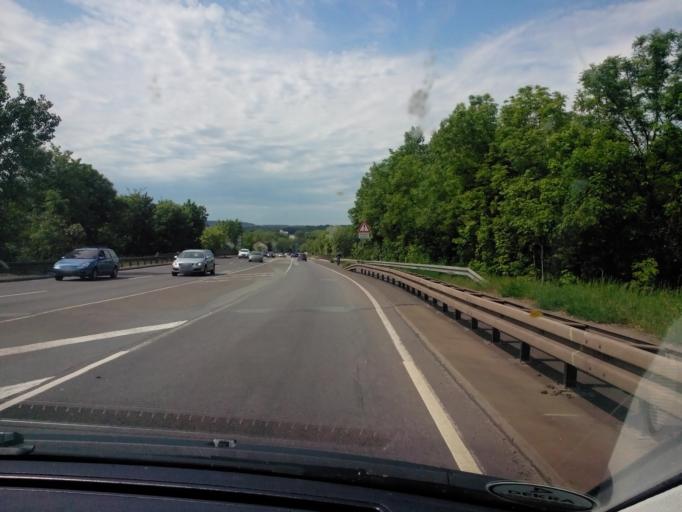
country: DE
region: Saarland
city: Dillingen
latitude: 49.3457
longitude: 6.7363
